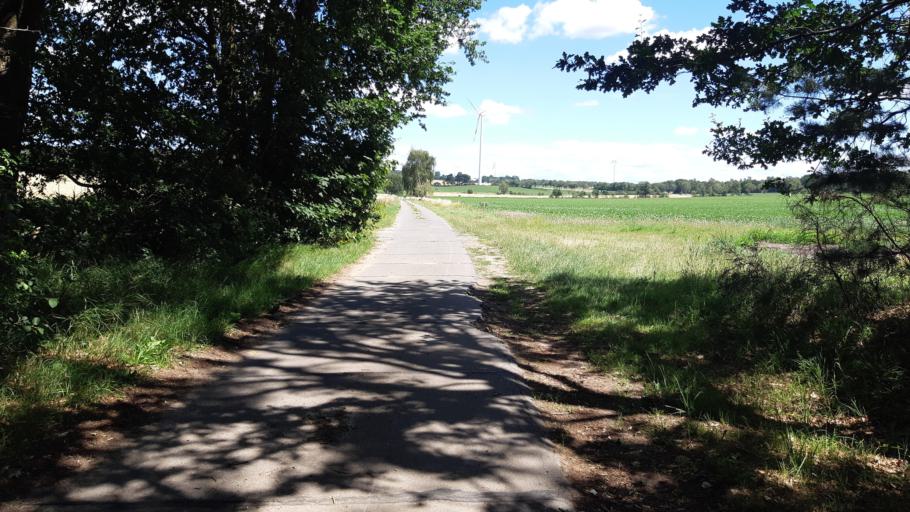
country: DE
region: Lower Saxony
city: Dahlem
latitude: 53.1921
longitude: 10.7638
